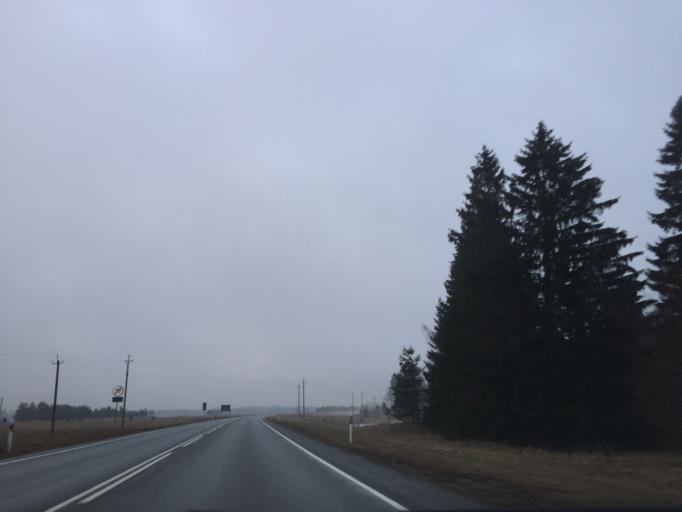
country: EE
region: Laeaene
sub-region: Lihula vald
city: Lihula
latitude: 58.6637
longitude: 23.7340
